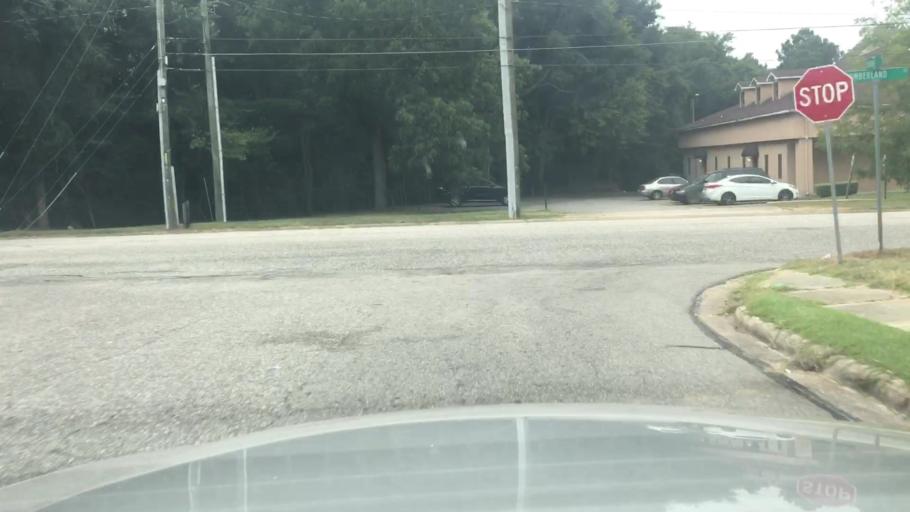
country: US
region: North Carolina
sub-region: Cumberland County
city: Fayetteville
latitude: 35.0669
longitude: -78.8870
